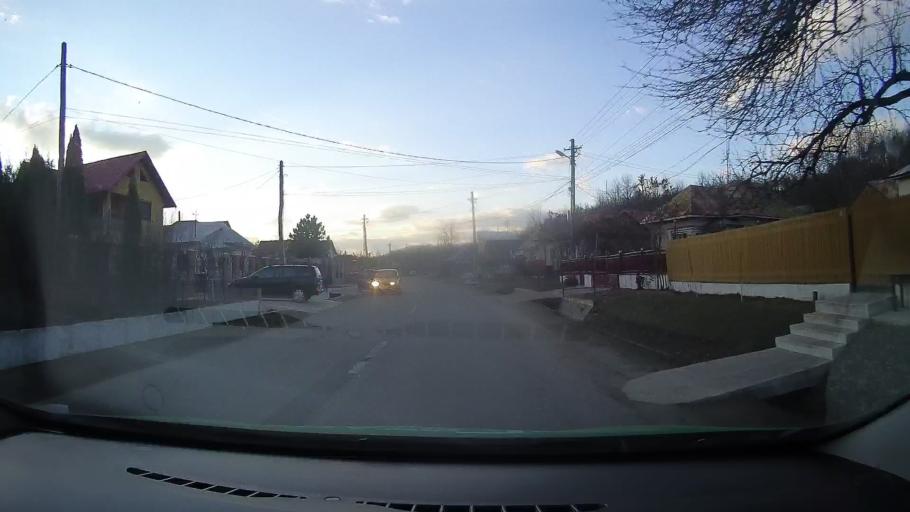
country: RO
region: Dambovita
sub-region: Comuna Gura Ocnitei
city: Adanca
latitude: 44.9336
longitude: 25.5973
